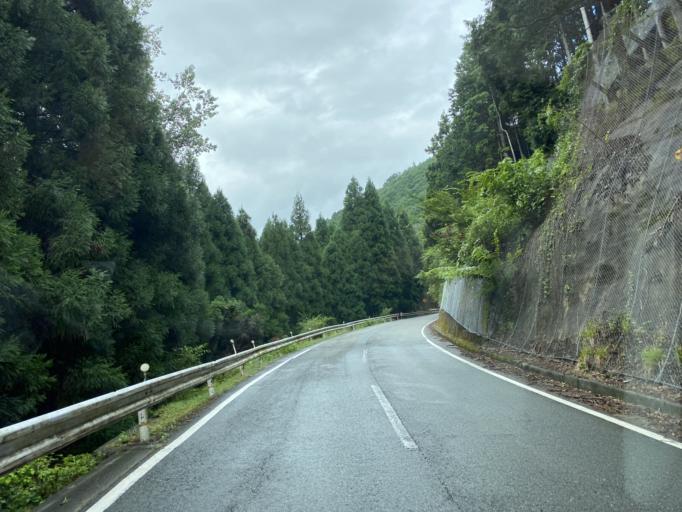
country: JP
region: Kyoto
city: Fukuchiyama
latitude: 35.3025
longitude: 134.9475
